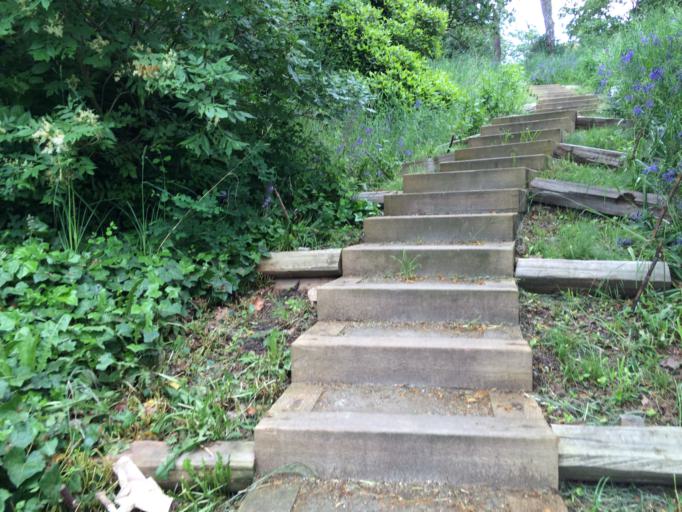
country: CA
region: British Columbia
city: Victoria
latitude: 48.4468
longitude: -123.3560
